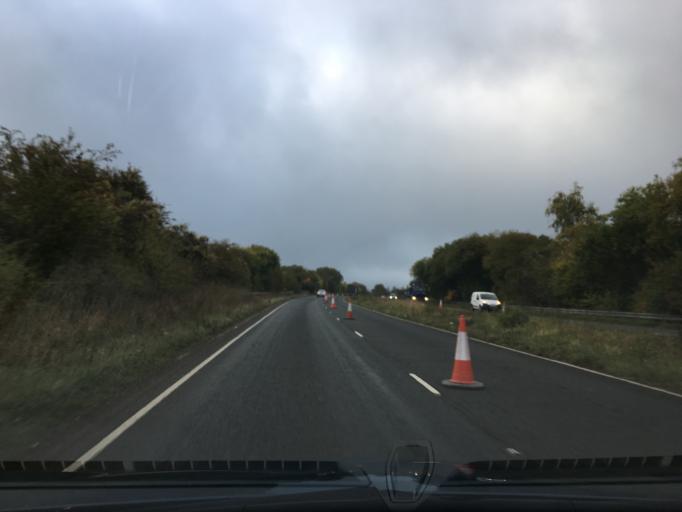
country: GB
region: England
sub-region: Hampshire
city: Alton
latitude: 51.1453
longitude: -0.9592
